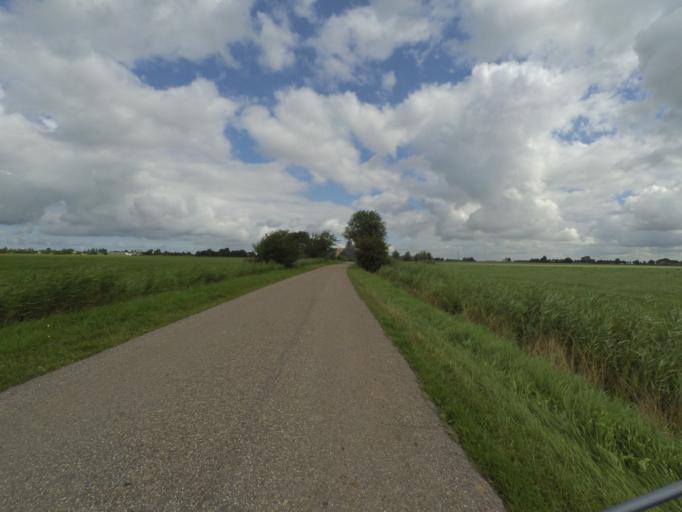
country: NL
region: Friesland
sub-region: Gemeente Kollumerland en Nieuwkruisland
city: Kollum
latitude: 53.2672
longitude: 6.1753
